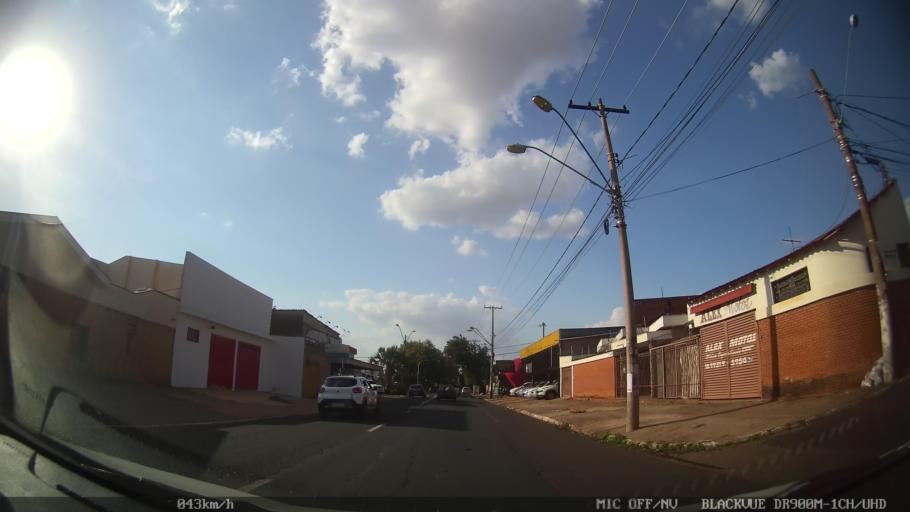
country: BR
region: Sao Paulo
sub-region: Ribeirao Preto
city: Ribeirao Preto
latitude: -21.1546
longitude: -47.8057
